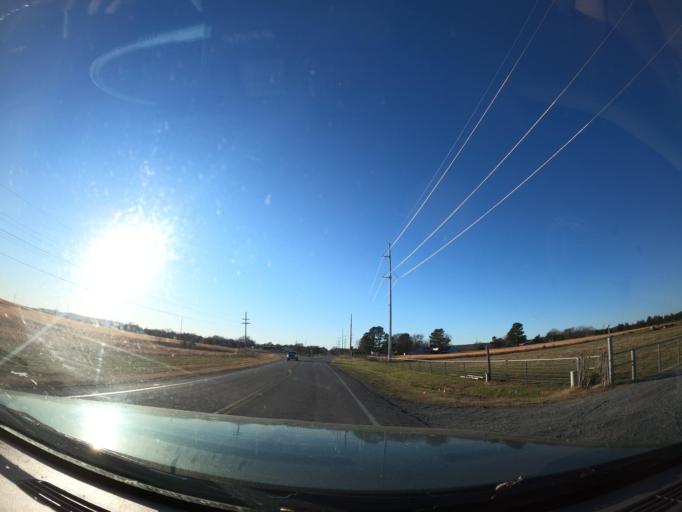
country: US
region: Oklahoma
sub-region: Latimer County
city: Wilburton
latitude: 34.9129
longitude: -95.4167
